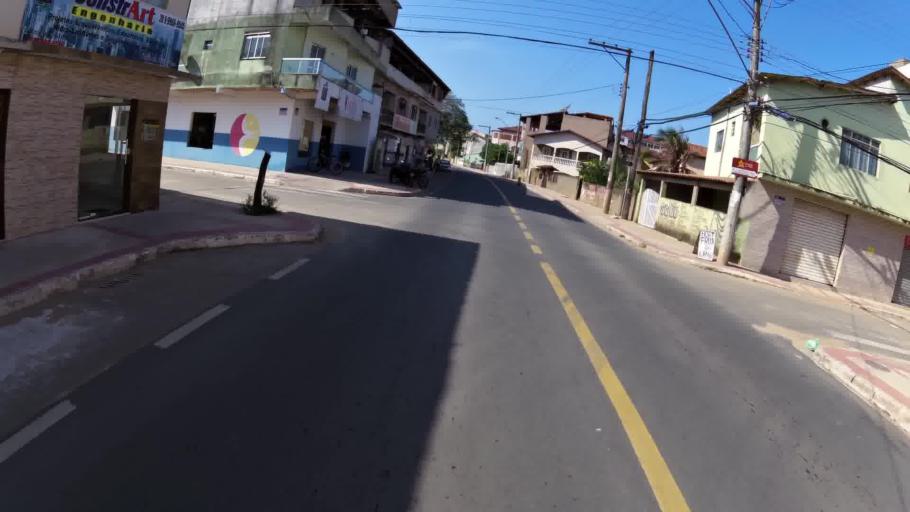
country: BR
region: Espirito Santo
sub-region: Piuma
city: Piuma
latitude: -20.8498
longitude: -40.7485
